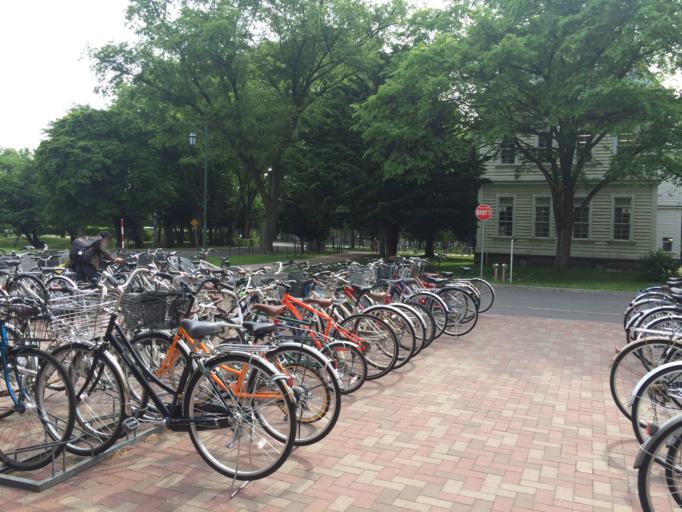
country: JP
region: Hokkaido
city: Sapporo
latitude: 43.0715
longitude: 141.3443
